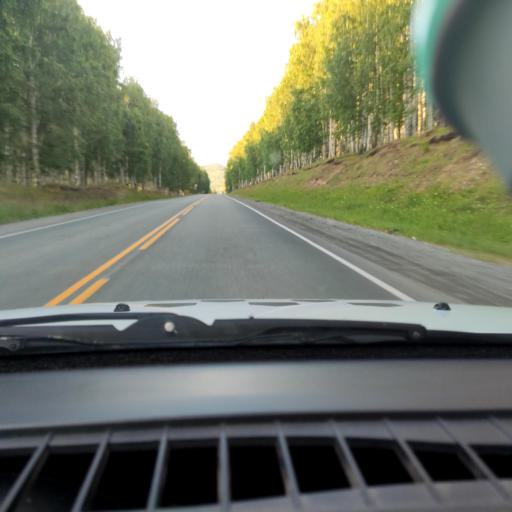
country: RU
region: Chelyabinsk
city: Karabash
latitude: 55.3305
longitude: 60.2321
